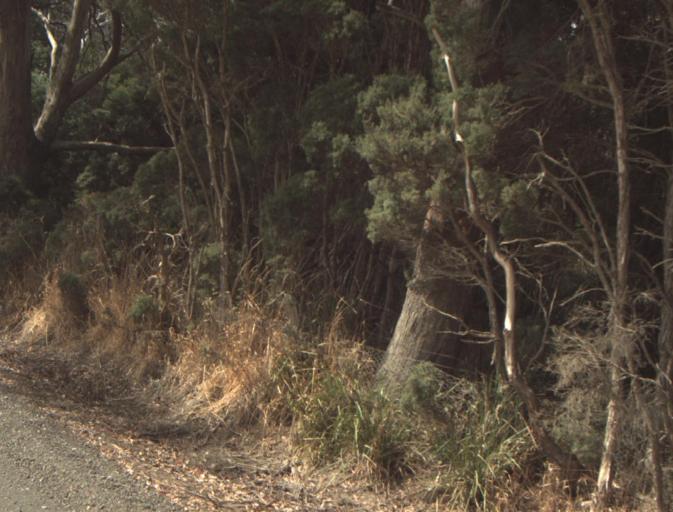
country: AU
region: Tasmania
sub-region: Launceston
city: Mayfield
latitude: -41.3033
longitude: 146.9953
